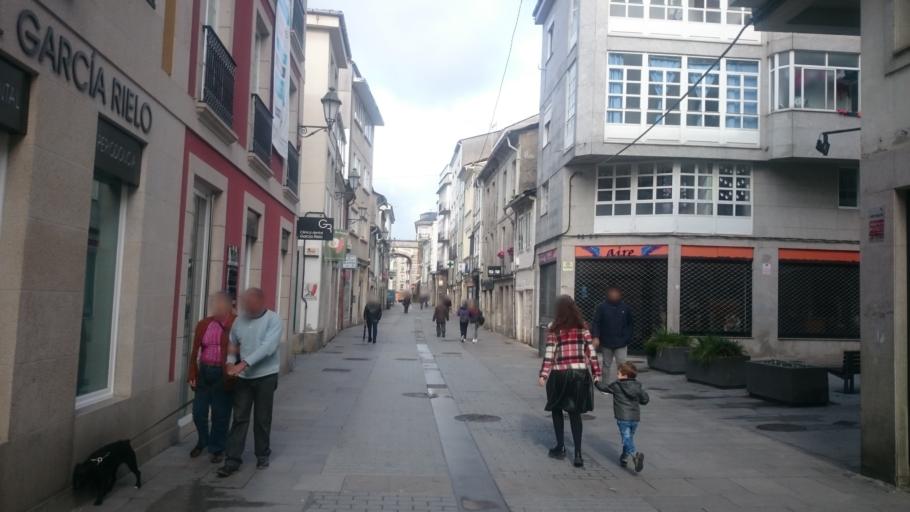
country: ES
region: Galicia
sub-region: Provincia de Lugo
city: Lugo
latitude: 43.0130
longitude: -7.5602
